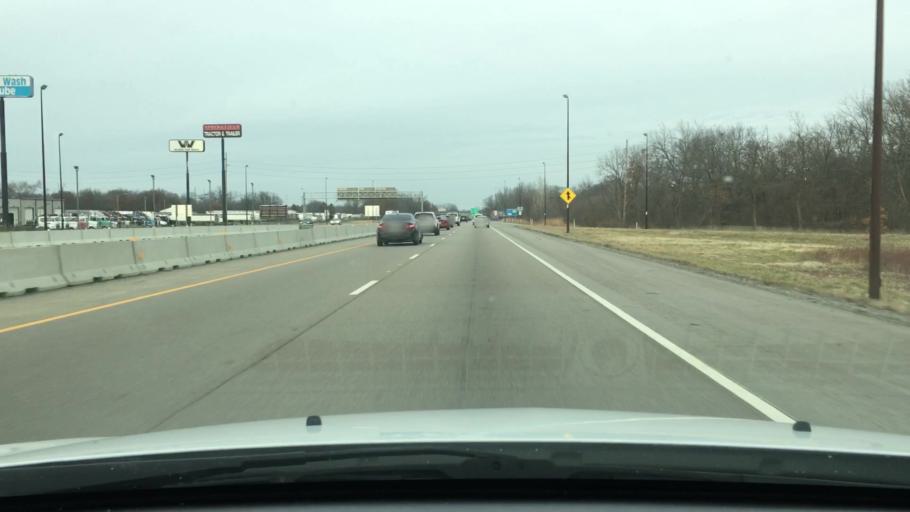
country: US
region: Illinois
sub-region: Sangamon County
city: Grandview
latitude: 39.7882
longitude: -89.5987
